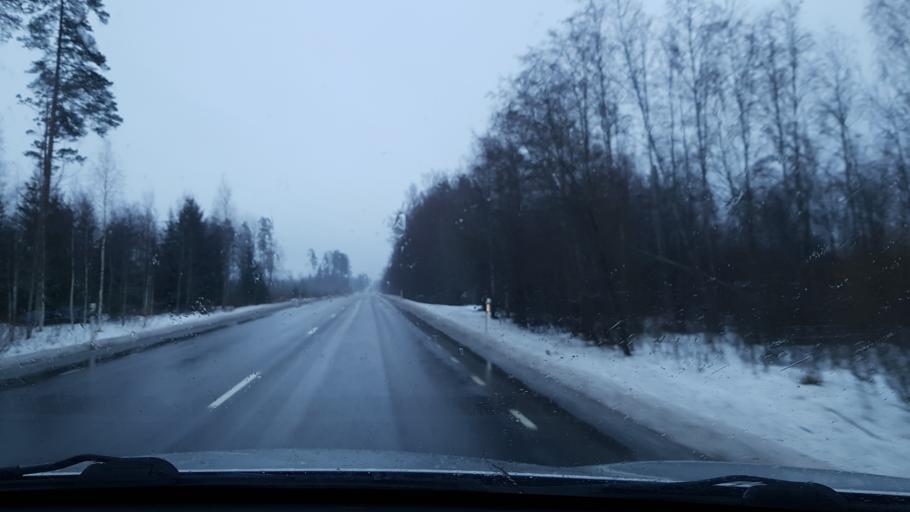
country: EE
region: Paernumaa
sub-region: Vaendra vald (alev)
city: Vandra
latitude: 58.8123
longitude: 25.1841
